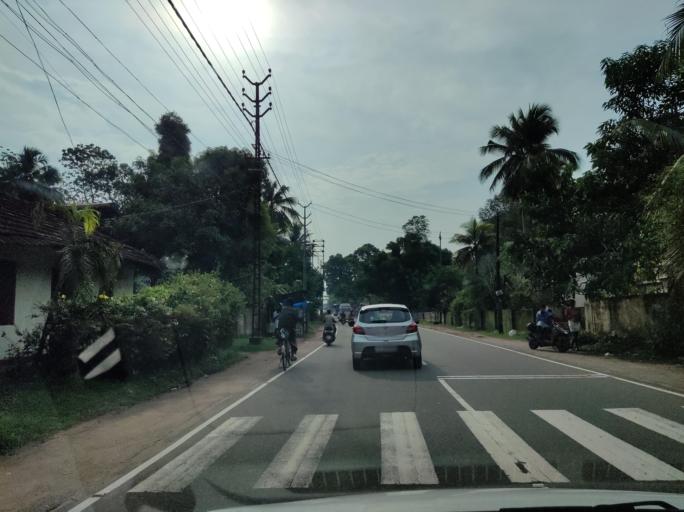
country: IN
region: Kerala
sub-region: Alappuzha
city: Kattanam
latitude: 9.1771
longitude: 76.5582
